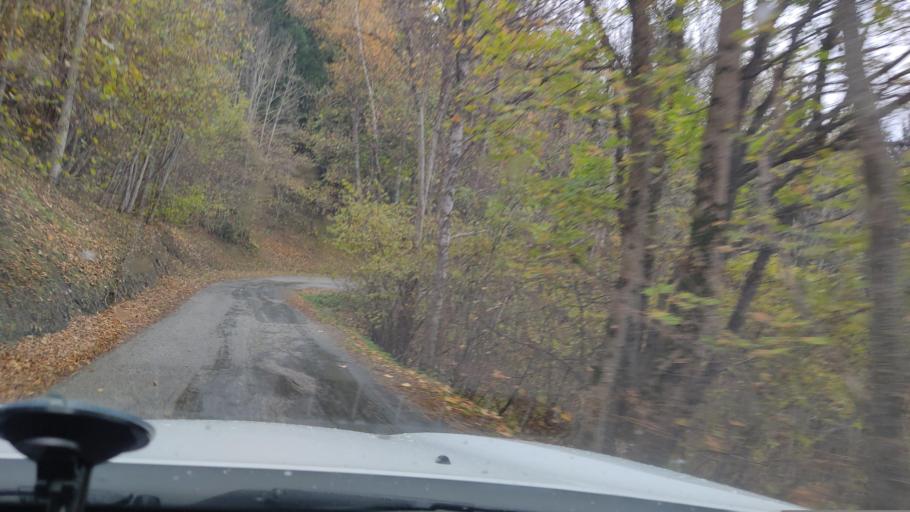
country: FR
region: Rhone-Alpes
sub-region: Departement de la Savoie
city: Bourg-Saint-Maurice
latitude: 45.6000
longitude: 6.7734
